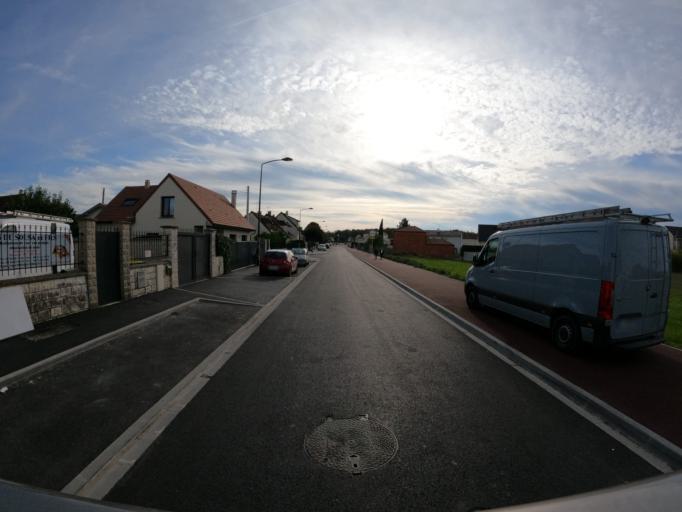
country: FR
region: Ile-de-France
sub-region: Departement de Seine-et-Marne
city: Pontault-Combault
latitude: 48.7925
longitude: 2.5987
